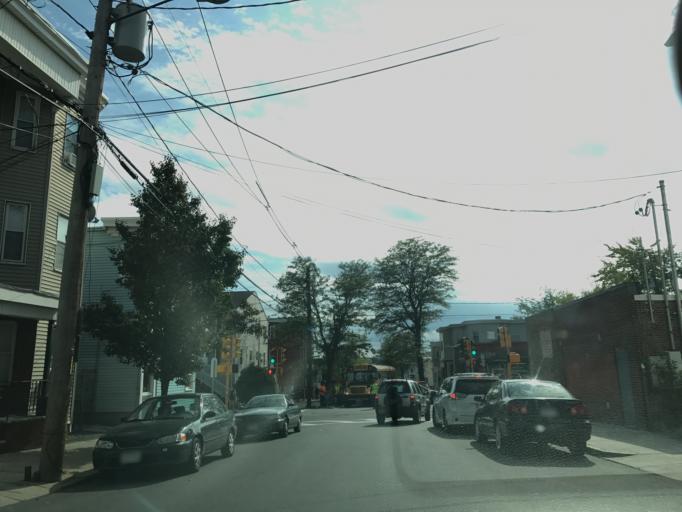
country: US
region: Massachusetts
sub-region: Suffolk County
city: Chelsea
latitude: 42.3893
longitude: -71.0300
